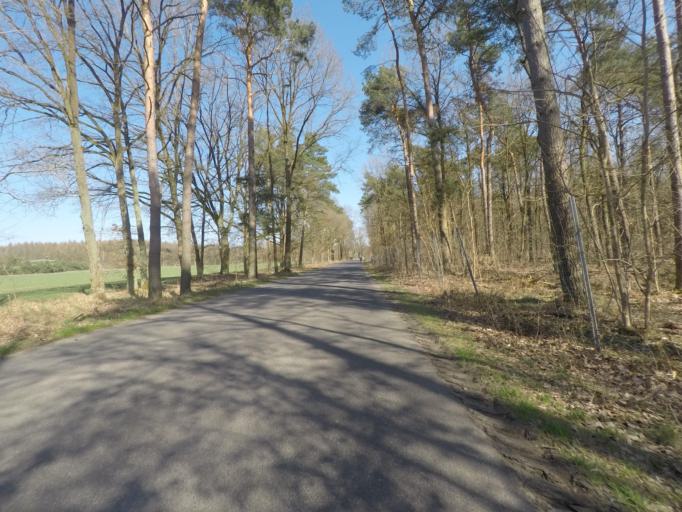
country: DE
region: Brandenburg
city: Melchow
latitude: 52.8643
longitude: 13.7086
